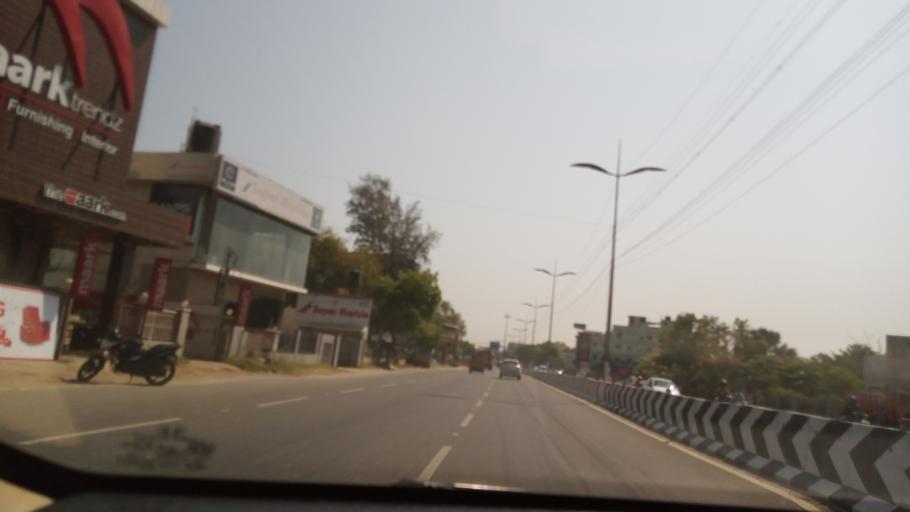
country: IN
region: Tamil Nadu
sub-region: Coimbatore
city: Irugur
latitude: 11.0456
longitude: 77.0501
